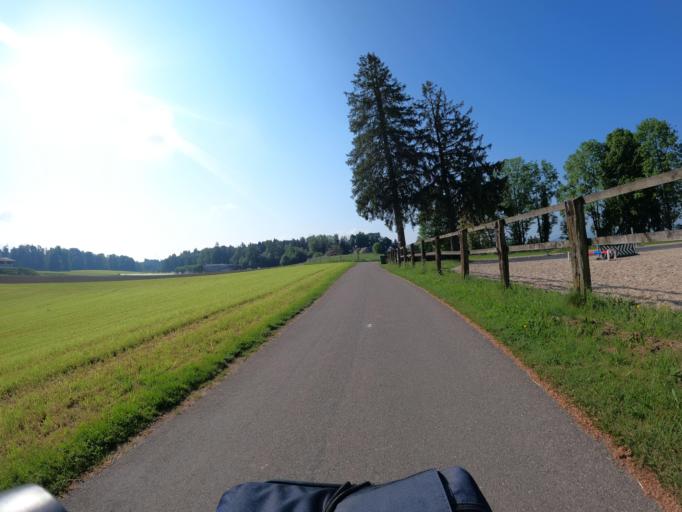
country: CH
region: Zurich
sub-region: Bezirk Affoltern
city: Mettmenstetten
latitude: 47.2382
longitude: 8.4735
